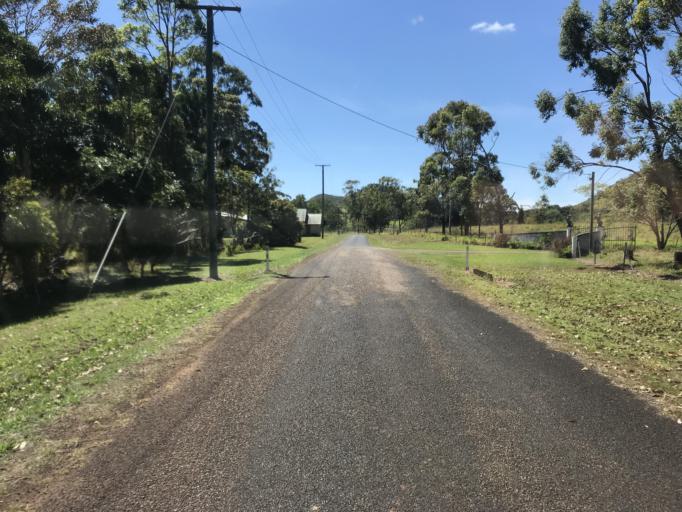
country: AU
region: Queensland
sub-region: Tablelands
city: Atherton
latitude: -17.2732
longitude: 145.5458
